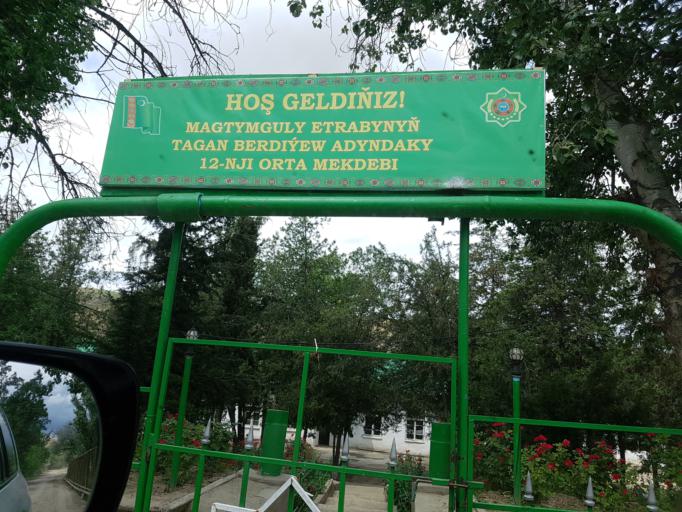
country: TM
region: Ahal
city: Baharly
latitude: 38.1933
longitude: 57.0065
